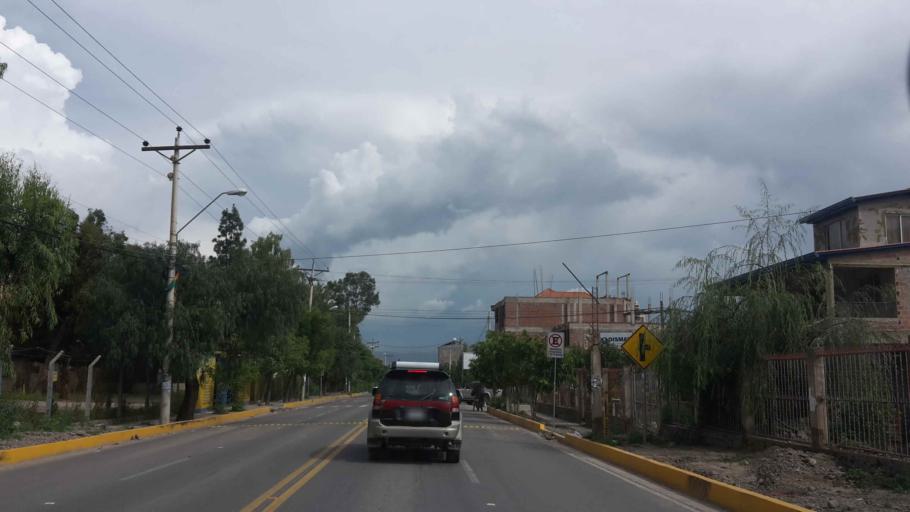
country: BO
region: Cochabamba
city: Cochabamba
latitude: -17.3491
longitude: -66.2573
